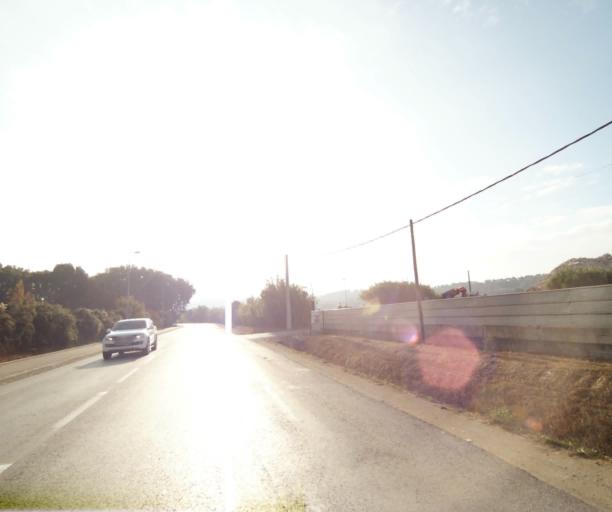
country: FR
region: Provence-Alpes-Cote d'Azur
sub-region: Departement des Bouches-du-Rhone
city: Saint-Victoret
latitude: 43.4168
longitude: 5.2622
